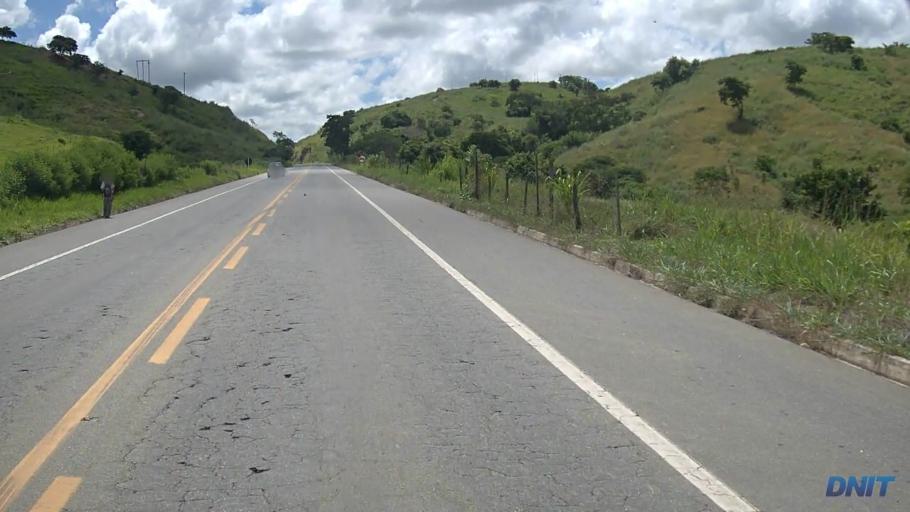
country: BR
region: Minas Gerais
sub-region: Governador Valadares
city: Governador Valadares
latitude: -18.8730
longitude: -41.9922
